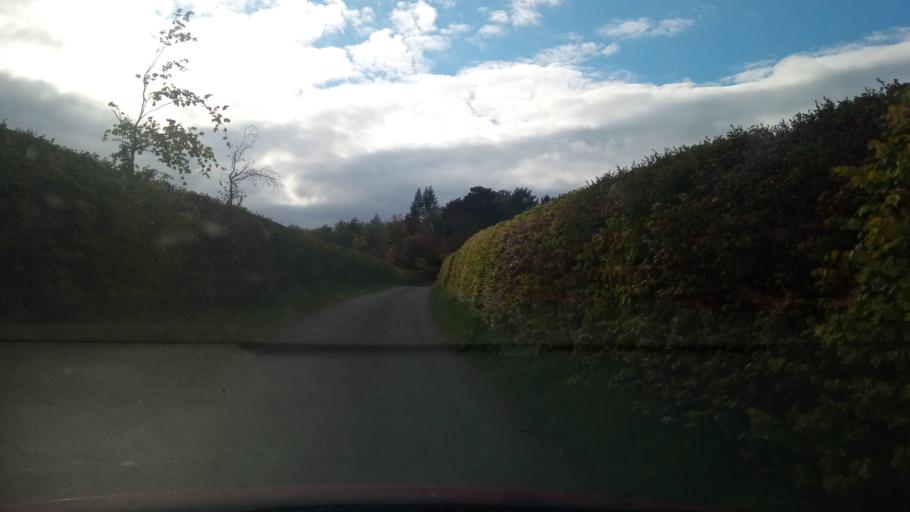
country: GB
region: Scotland
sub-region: The Scottish Borders
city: Saint Boswells
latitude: 55.5147
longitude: -2.6721
